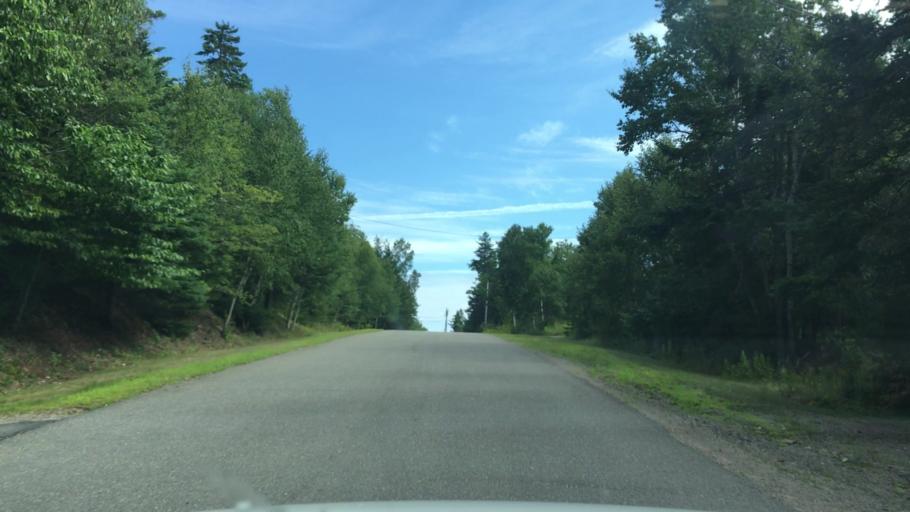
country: US
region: Maine
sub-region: Washington County
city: Eastport
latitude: 44.9343
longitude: -67.0462
